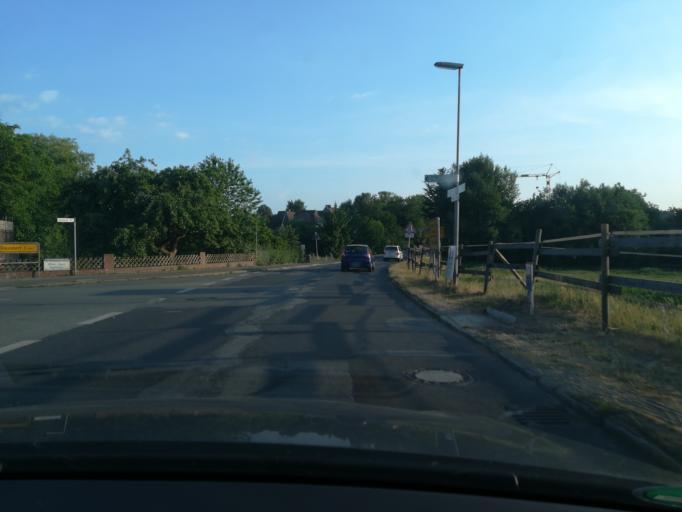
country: DE
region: Schleswig-Holstein
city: Grossensee
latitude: 53.6131
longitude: 10.3414
